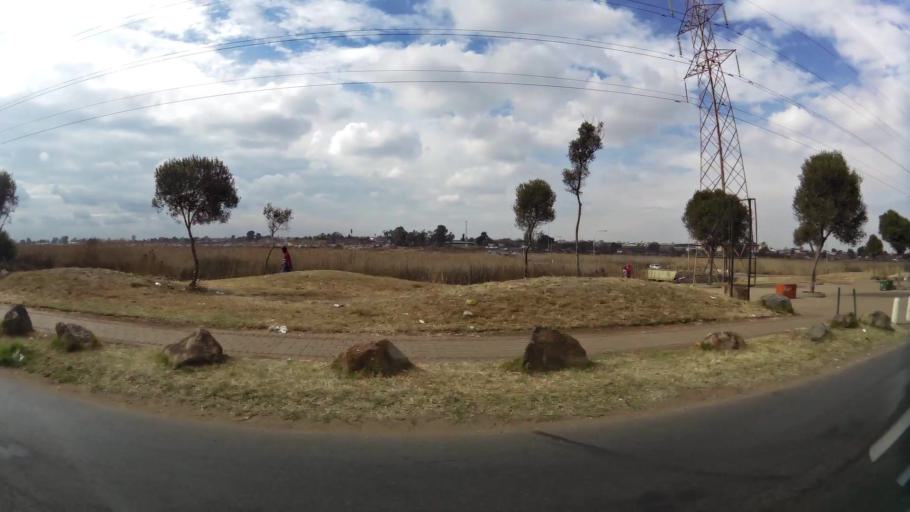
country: ZA
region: Gauteng
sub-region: City of Johannesburg Metropolitan Municipality
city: Soweto
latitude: -26.2719
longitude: 27.8815
